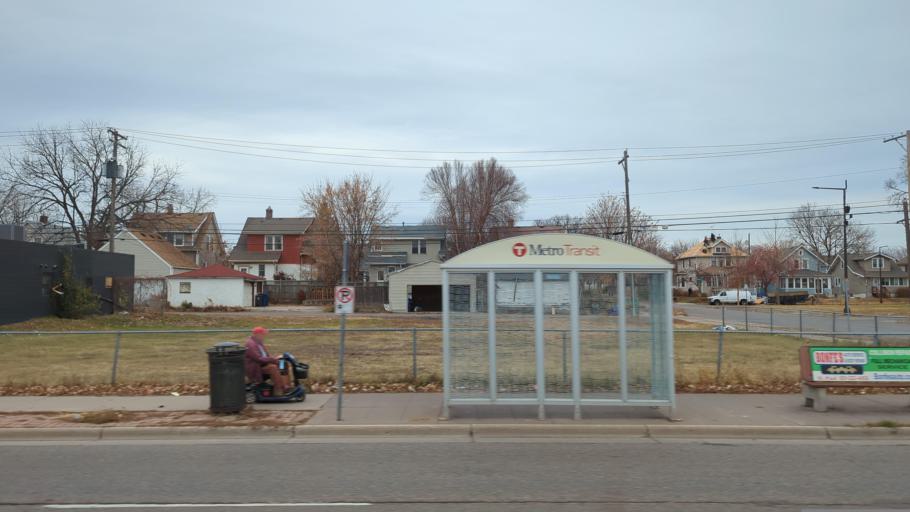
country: US
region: Minnesota
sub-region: Ramsey County
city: Falcon Heights
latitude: 44.9559
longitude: -93.1597
